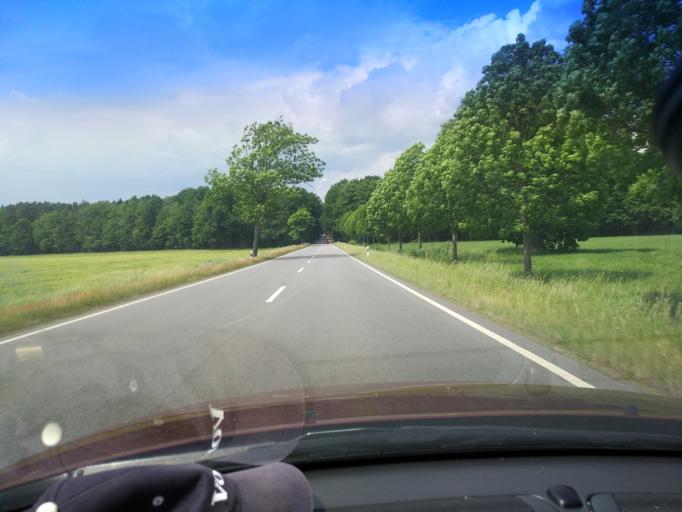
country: DE
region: Saxony
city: Niesky
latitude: 51.2748
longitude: 14.8312
